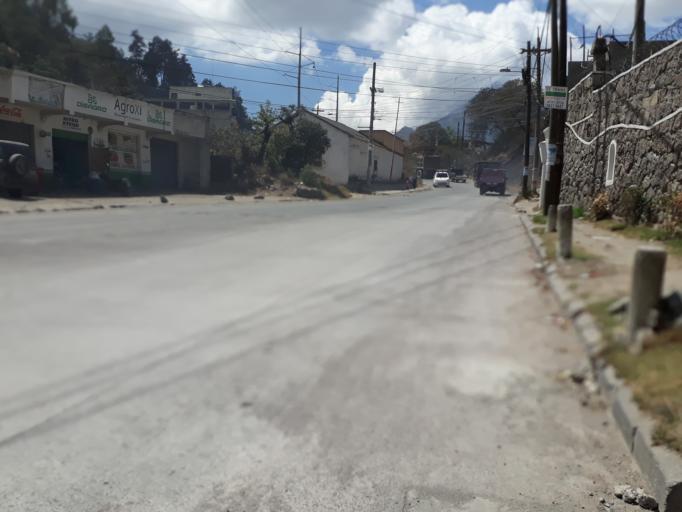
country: GT
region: Quetzaltenango
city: Quetzaltenango
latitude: 14.8241
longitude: -91.5367
